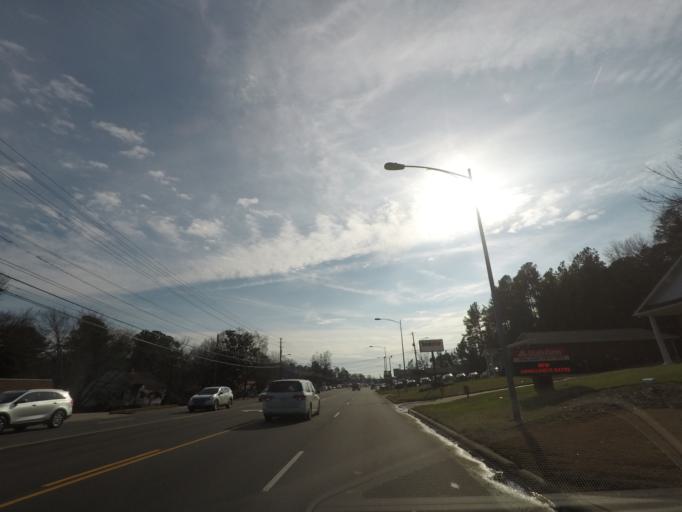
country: US
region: North Carolina
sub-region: Durham County
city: Durham
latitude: 36.0580
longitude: -78.9033
